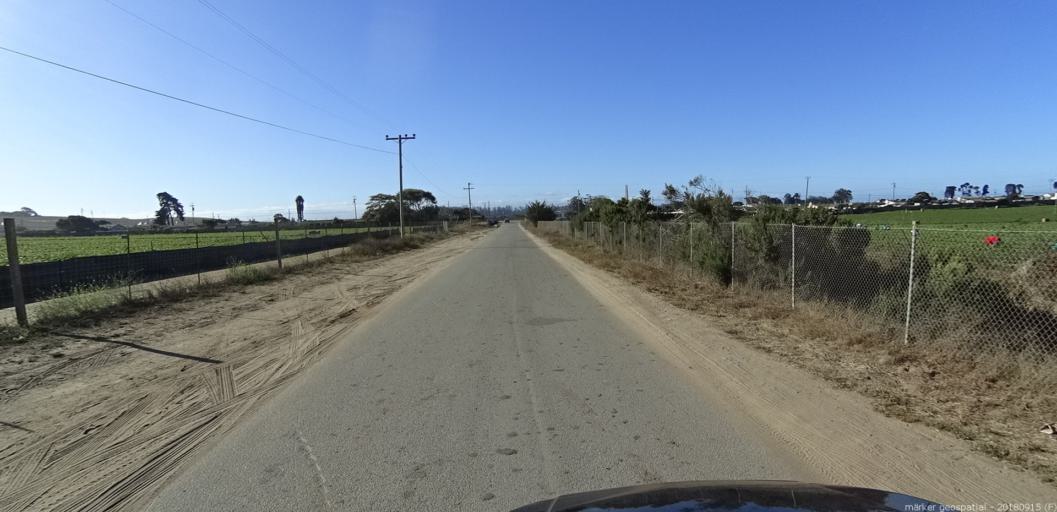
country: US
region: California
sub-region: Monterey County
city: Elkhorn
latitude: 36.8331
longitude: -121.7745
